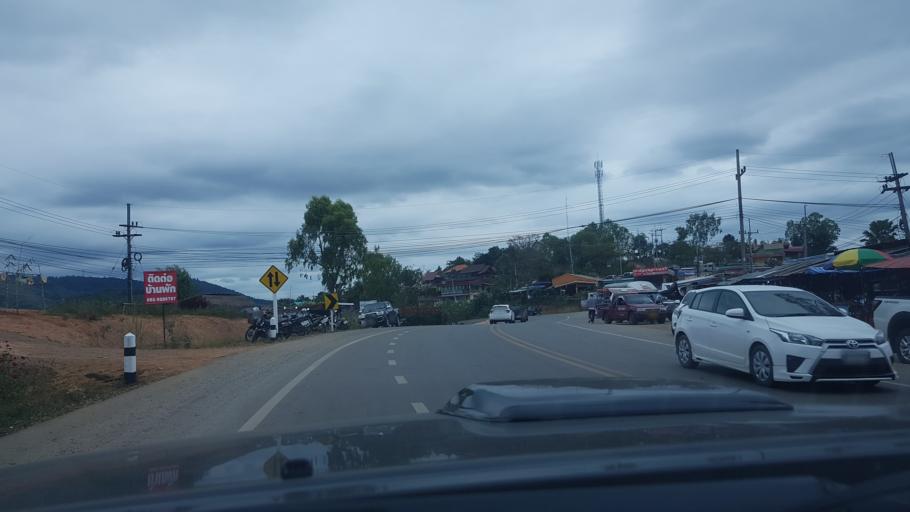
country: TH
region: Phetchabun
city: Khao Kho
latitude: 16.5684
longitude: 101.0060
